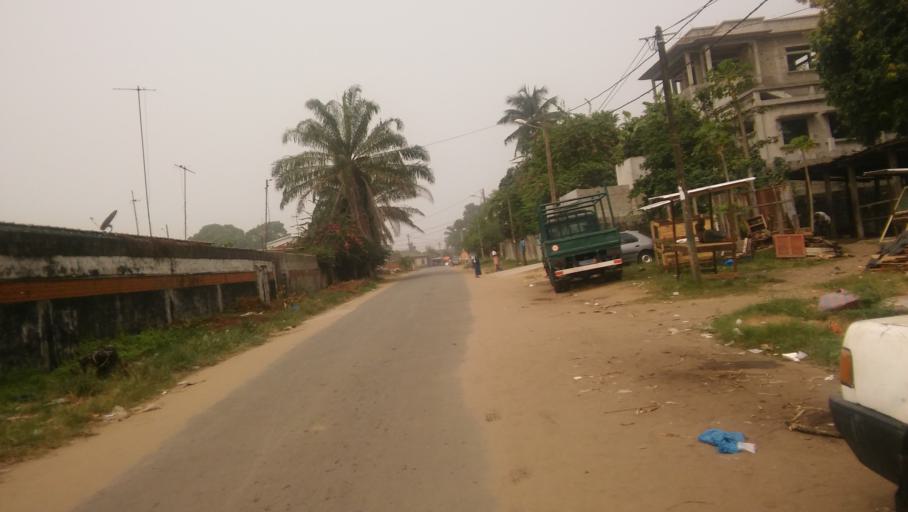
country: CI
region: Sud-Comoe
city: Grand-Bassam
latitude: 5.2121
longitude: -3.7316
